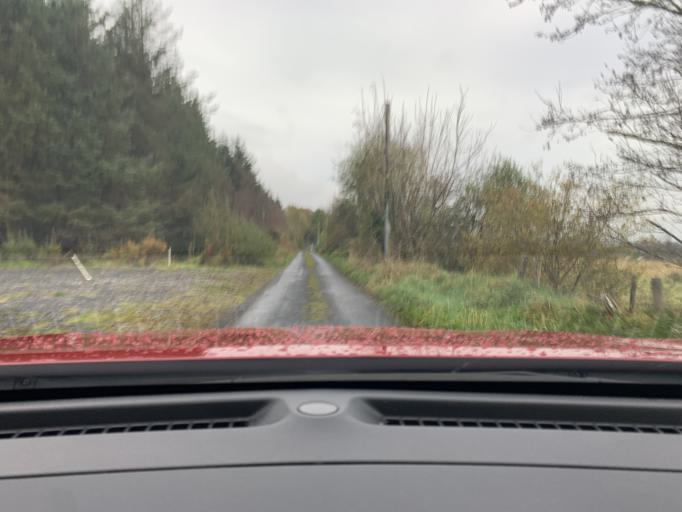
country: IE
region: Connaught
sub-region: Roscommon
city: Ballaghaderreen
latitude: 53.9191
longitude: -8.5578
